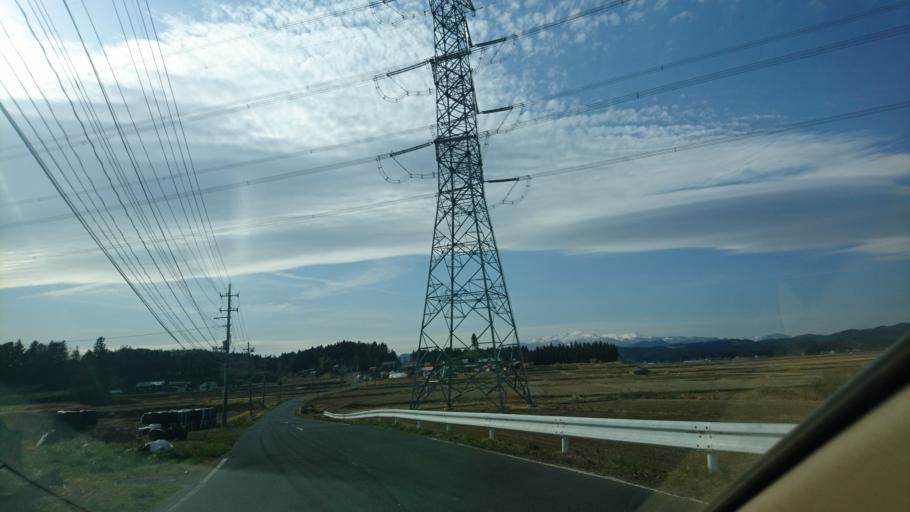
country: JP
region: Iwate
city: Ichinoseki
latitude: 38.8128
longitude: 141.0260
